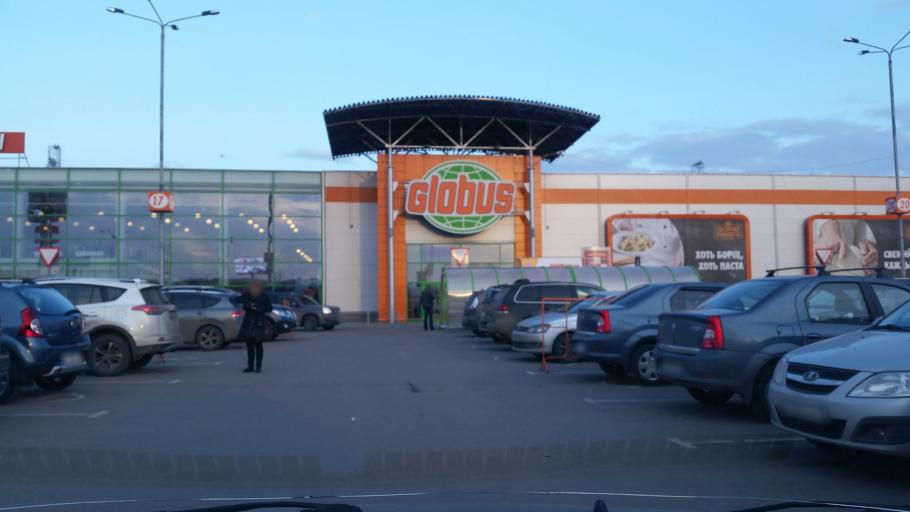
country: RU
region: Moskovskaya
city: Arkhangel'skoye
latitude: 55.8024
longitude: 37.2986
